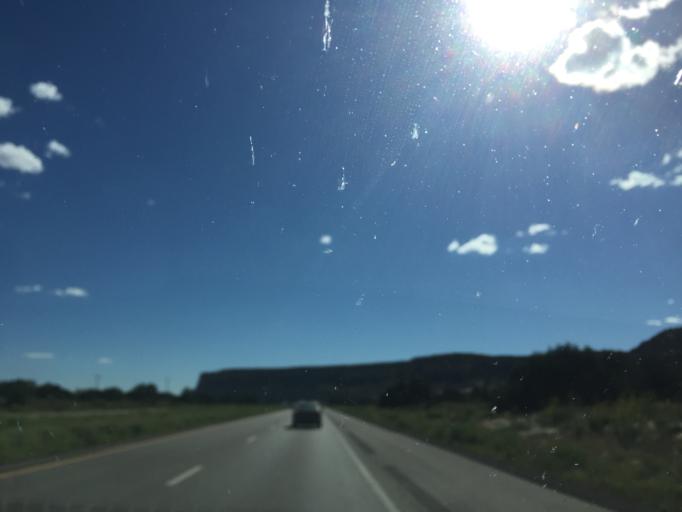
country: US
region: Arizona
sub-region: Apache County
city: Houck
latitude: 35.3778
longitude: -109.0269
